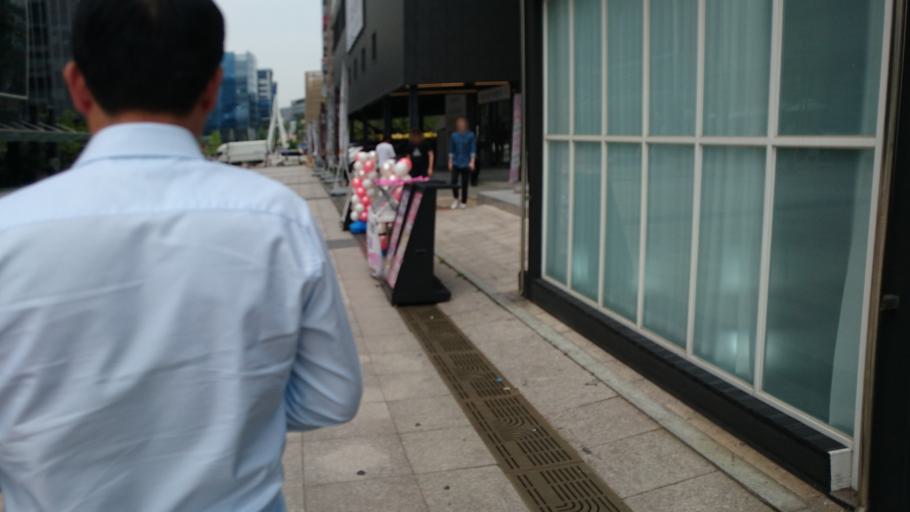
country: KR
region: Gyeonggi-do
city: Seongnam-si
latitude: 37.3963
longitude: 127.1113
